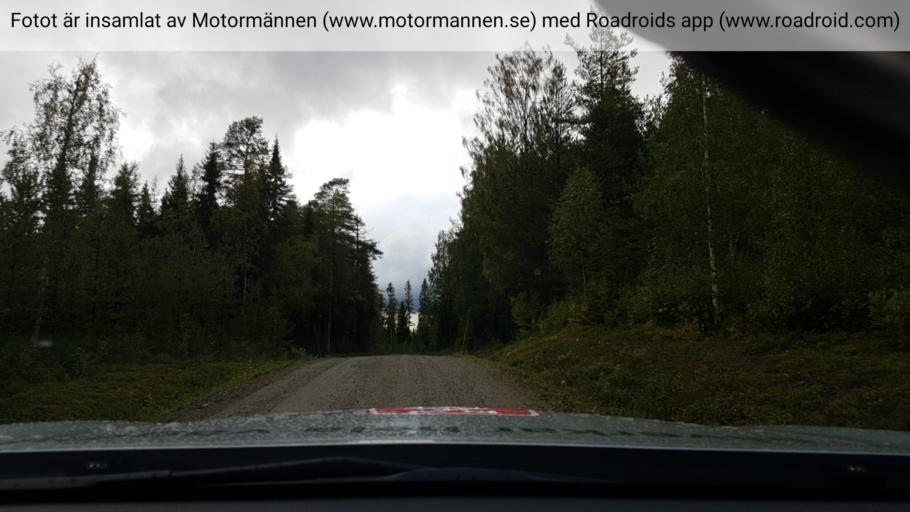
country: SE
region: Vaesterbotten
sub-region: Asele Kommun
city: Asele
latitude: 64.1482
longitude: 16.9340
